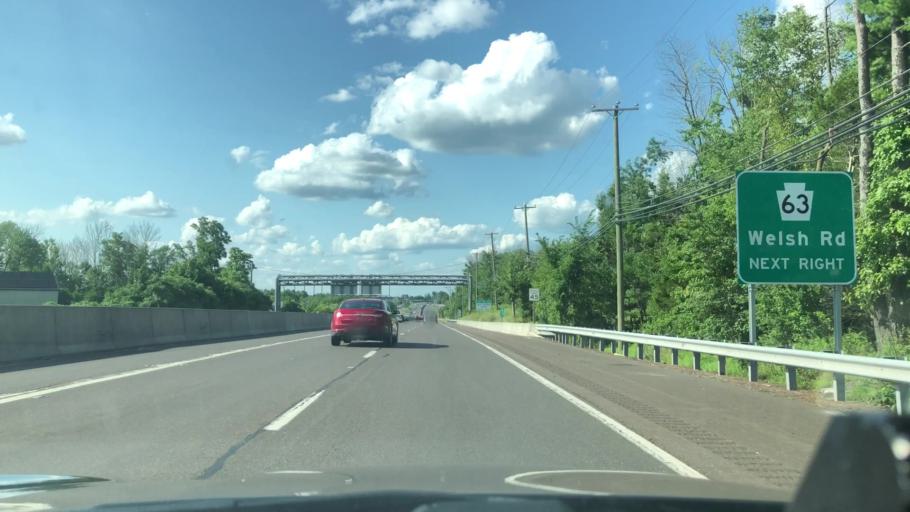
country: US
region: Pennsylvania
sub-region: Montgomery County
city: Spring House
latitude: 40.1991
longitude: -75.2239
